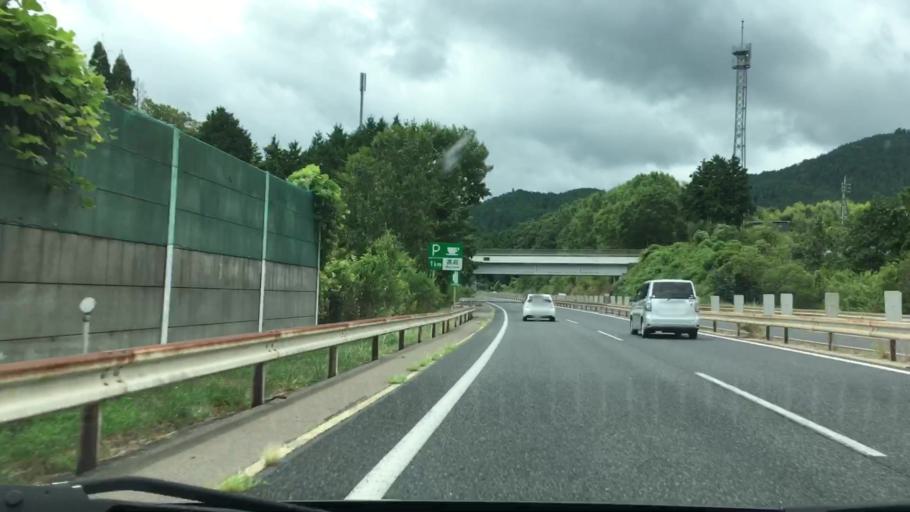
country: JP
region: Okayama
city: Takahashi
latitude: 35.0200
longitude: 133.7328
